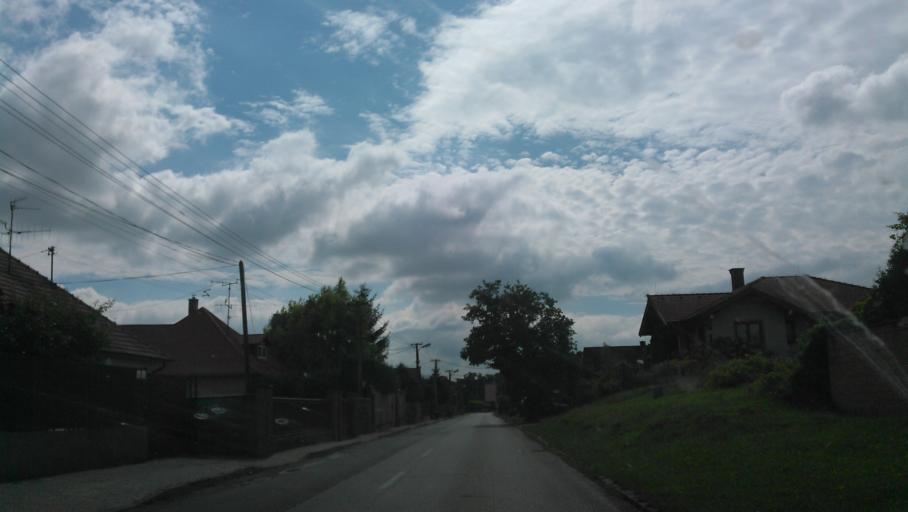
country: SK
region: Bratislavsky
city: Dunajska Luzna
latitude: 48.1535
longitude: 17.2893
